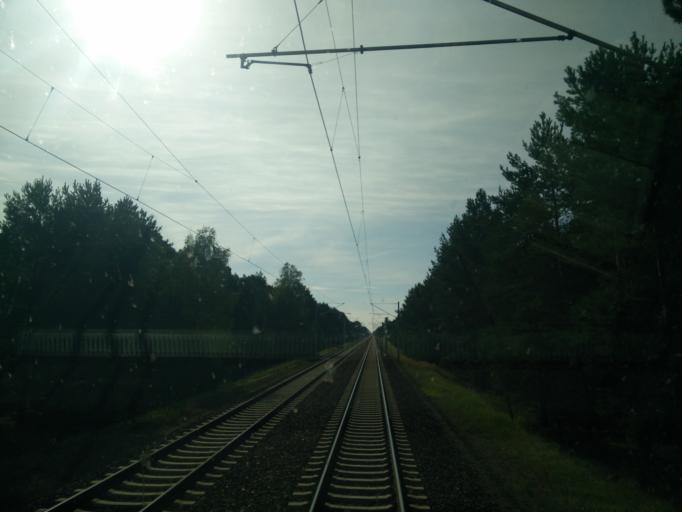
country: DE
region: Brandenburg
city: Kasel-Golzig
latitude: 52.0156
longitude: 13.7397
